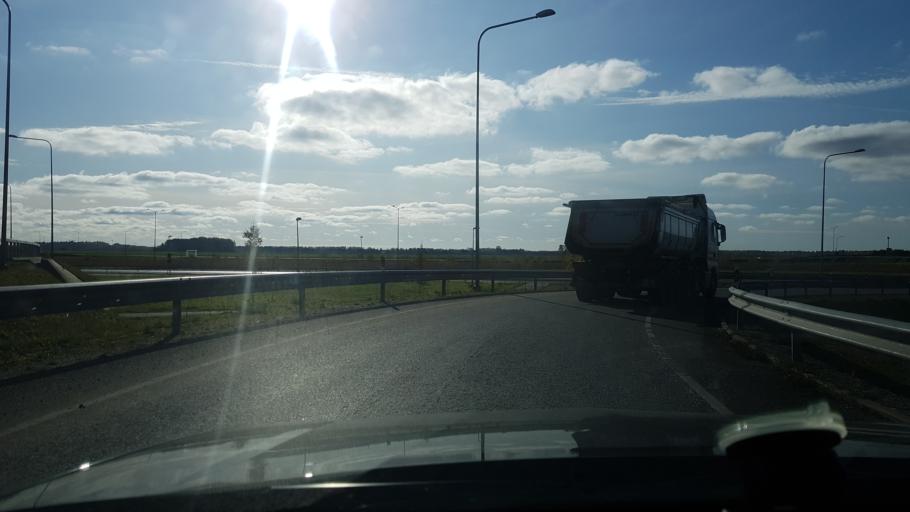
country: EE
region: Laeaene-Virumaa
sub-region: Haljala vald
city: Haljala
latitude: 59.4249
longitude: 26.2721
